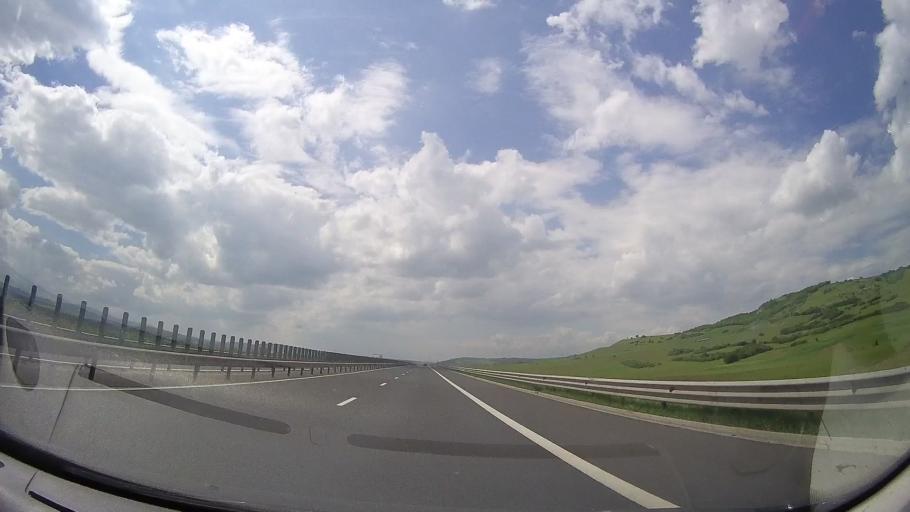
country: RO
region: Sibiu
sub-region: Oras Miercurea Sibiului
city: Miercurea Sibiului
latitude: 45.8927
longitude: 23.8240
